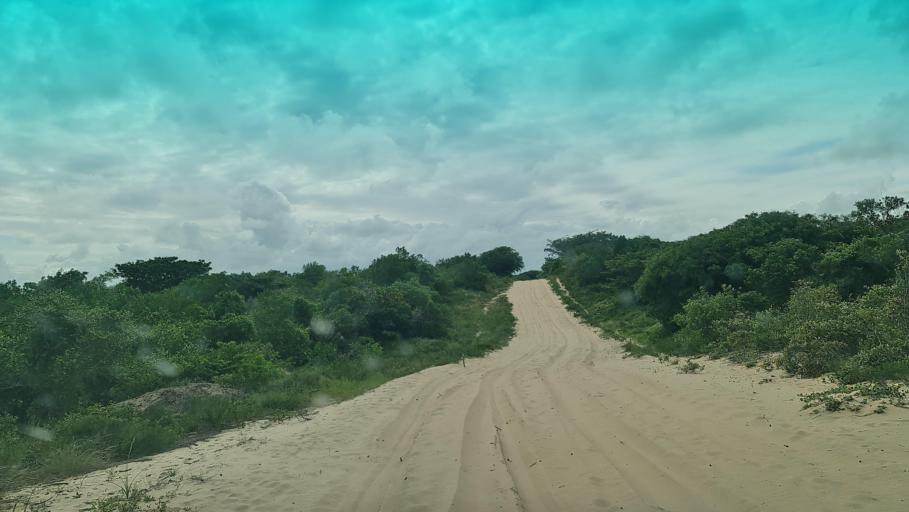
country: MZ
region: Maputo
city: Manhica
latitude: -25.4373
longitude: 32.9165
